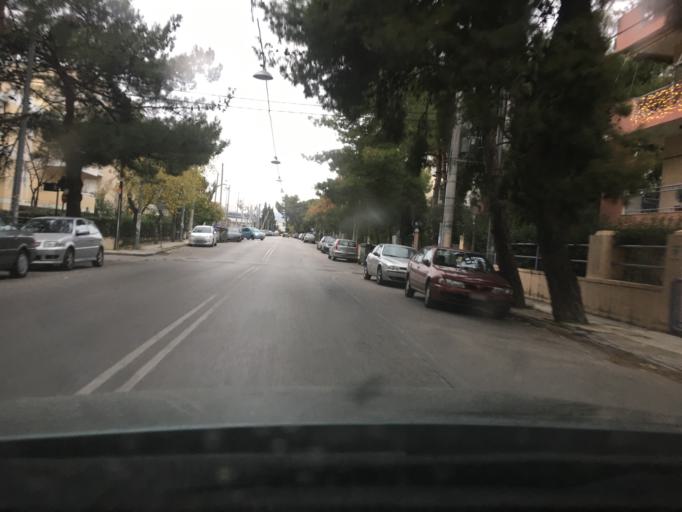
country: GR
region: Attica
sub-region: Nomarchia Athinas
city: Vrilissia
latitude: 38.0322
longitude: 23.8268
